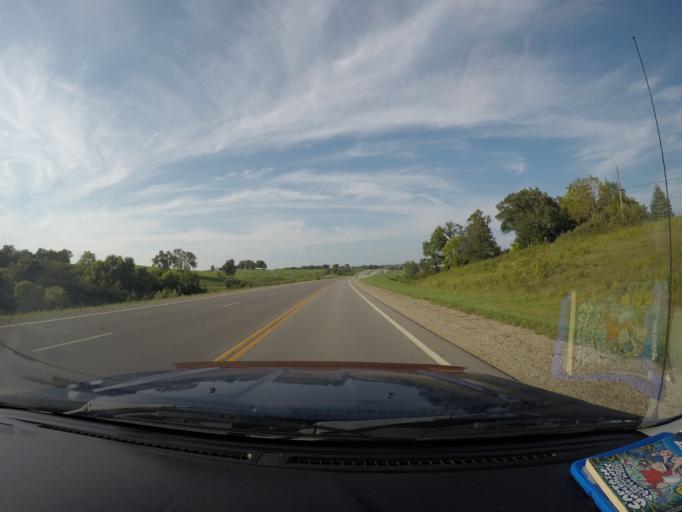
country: US
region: Kansas
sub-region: Atchison County
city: Atchison
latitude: 39.5335
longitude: -95.1329
